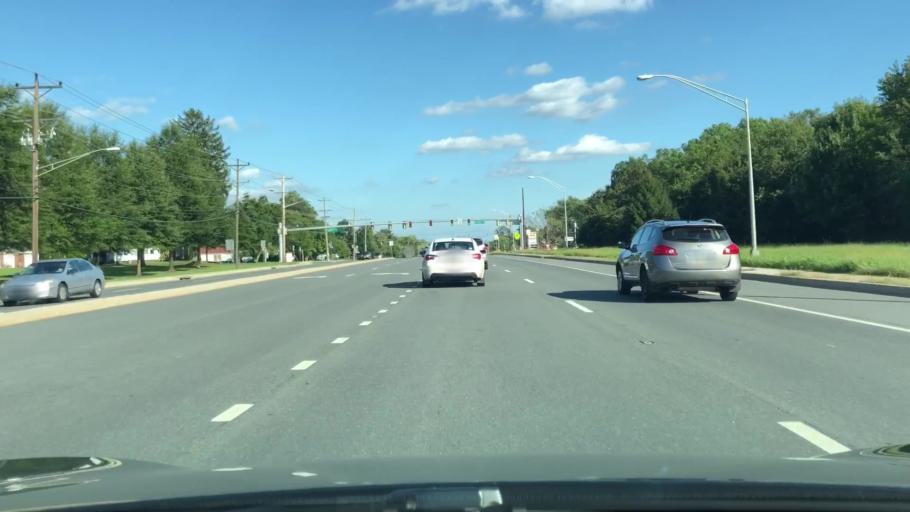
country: US
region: Delaware
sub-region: New Castle County
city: Bellefonte
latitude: 39.8286
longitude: -75.5261
